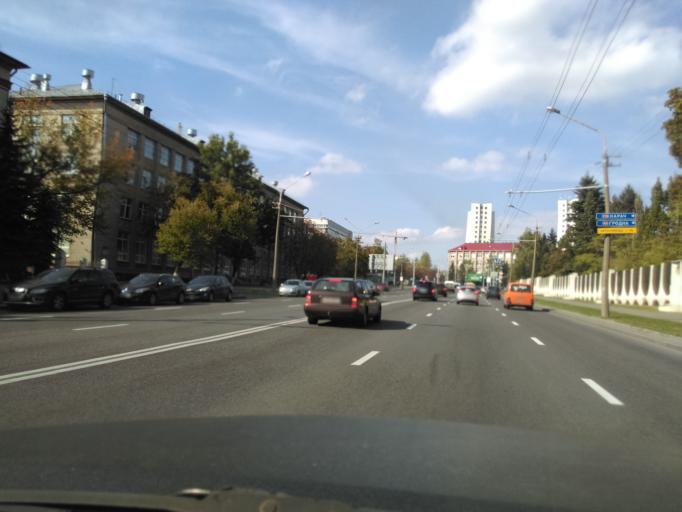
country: BY
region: Minsk
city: Minsk
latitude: 53.9135
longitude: 27.6058
